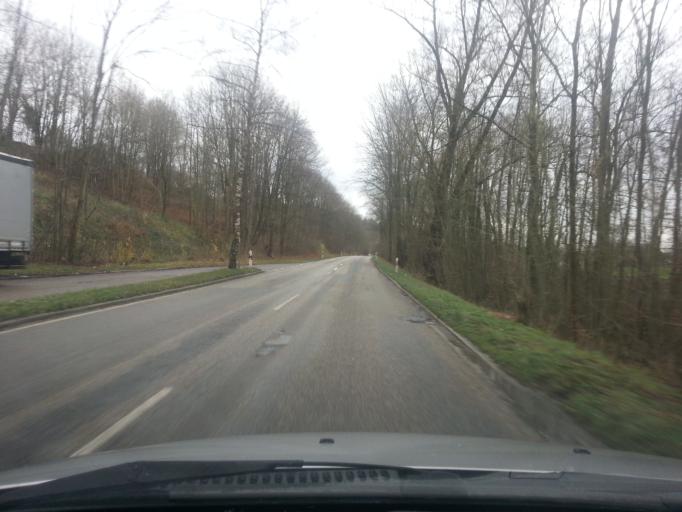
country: DE
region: Baden-Wuerttemberg
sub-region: Regierungsbezirk Stuttgart
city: Ittlingen
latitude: 49.2090
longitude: 8.9318
